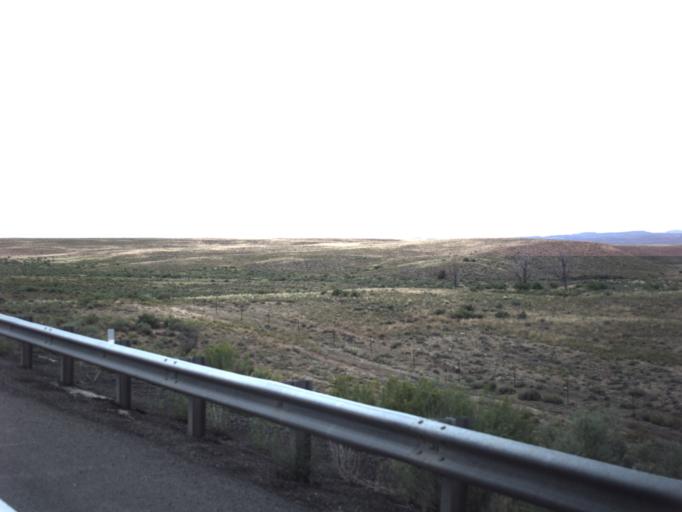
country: US
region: Utah
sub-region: Carbon County
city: East Carbon City
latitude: 39.5217
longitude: -110.5640
